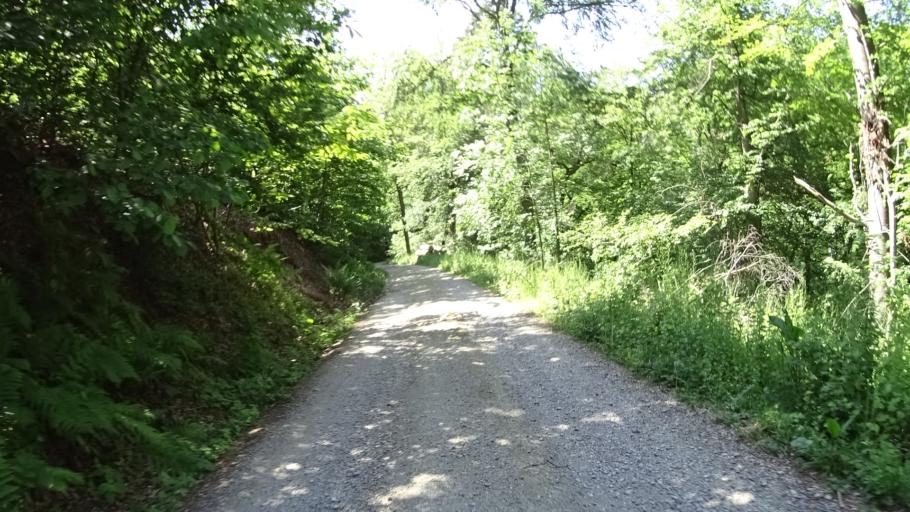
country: DE
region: Baden-Wuerttemberg
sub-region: Karlsruhe Region
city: Schriesheim
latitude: 49.4747
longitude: 8.6870
